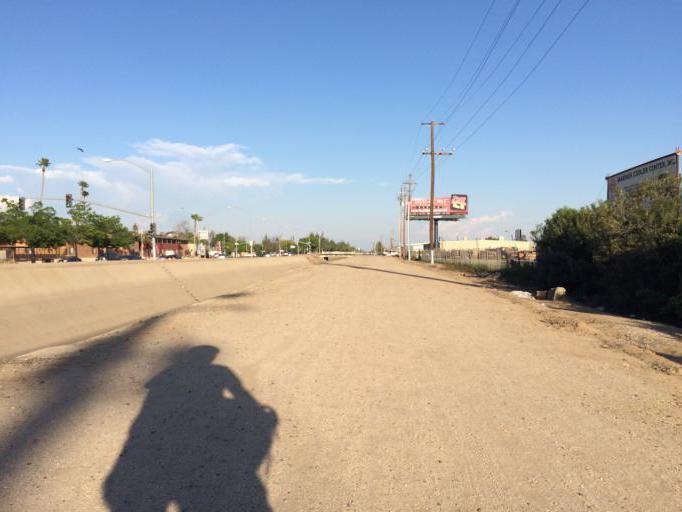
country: US
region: California
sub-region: Fresno County
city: Fresno
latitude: 36.7648
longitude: -119.7481
